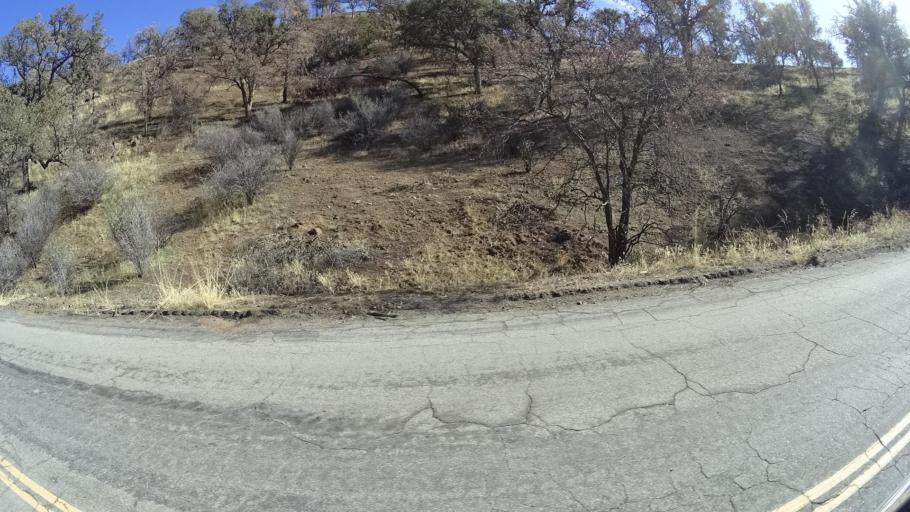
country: US
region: California
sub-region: Kern County
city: Bodfish
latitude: 35.4501
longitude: -118.5285
